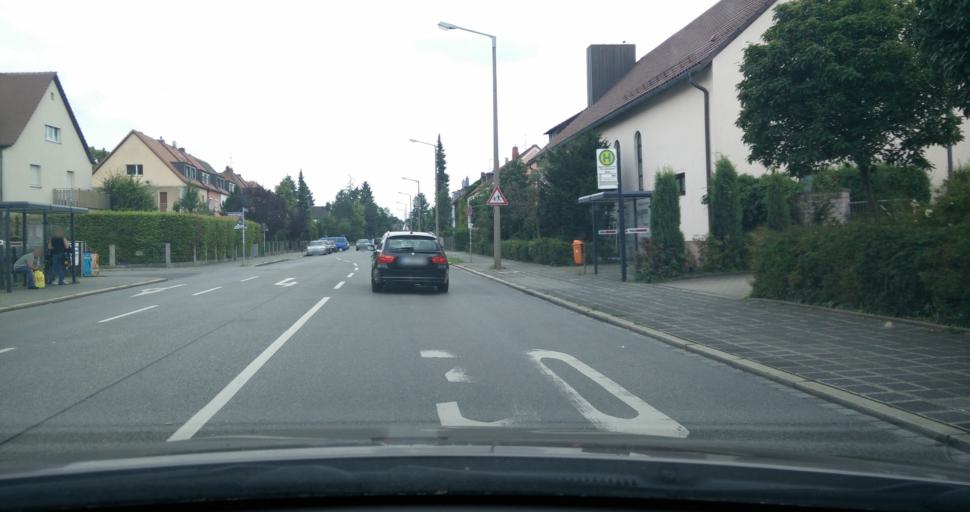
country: DE
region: Bavaria
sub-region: Regierungsbezirk Mittelfranken
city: Nuernberg
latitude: 49.4417
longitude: 11.1237
